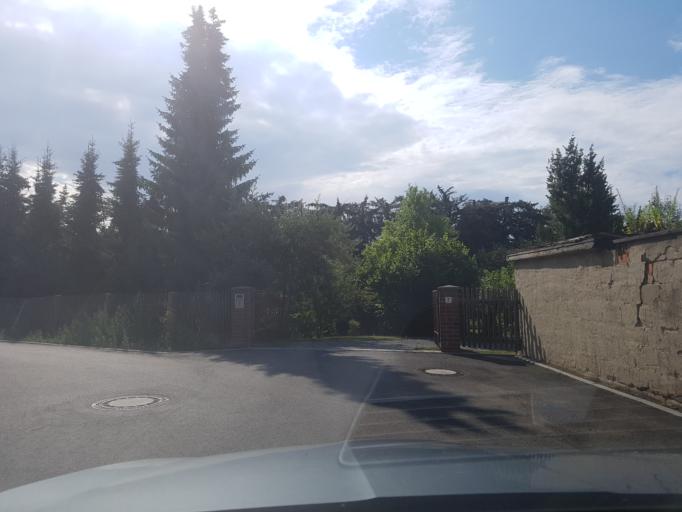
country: DE
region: Brandenburg
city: Doberlug-Kirchhain
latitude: 51.6119
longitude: 13.5457
